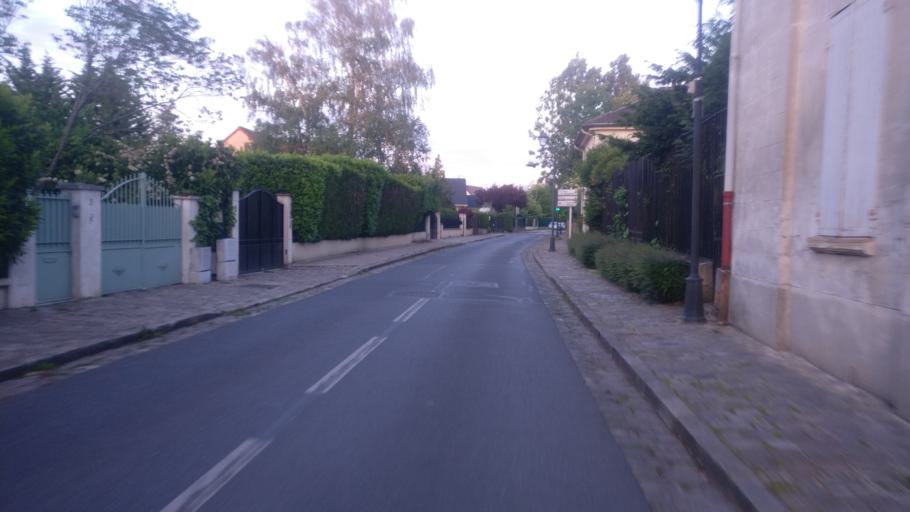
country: FR
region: Ile-de-France
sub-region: Departement du Val-de-Marne
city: Santeny
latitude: 48.7359
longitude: 2.5546
